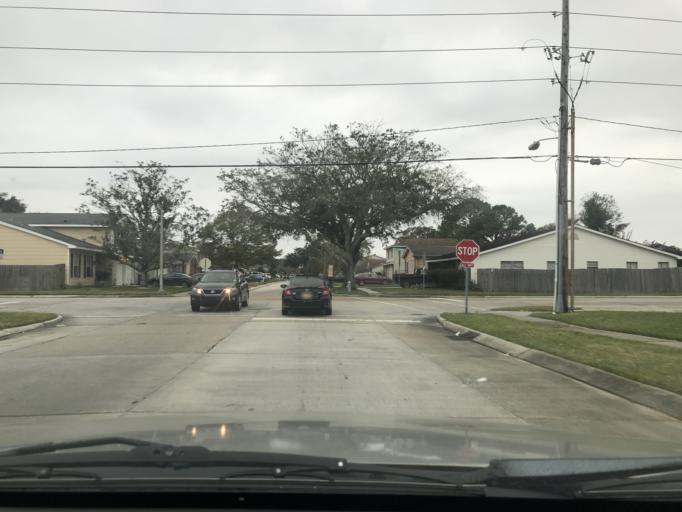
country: US
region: Louisiana
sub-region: Jefferson Parish
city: Woodmere
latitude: 29.8577
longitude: -90.0732
